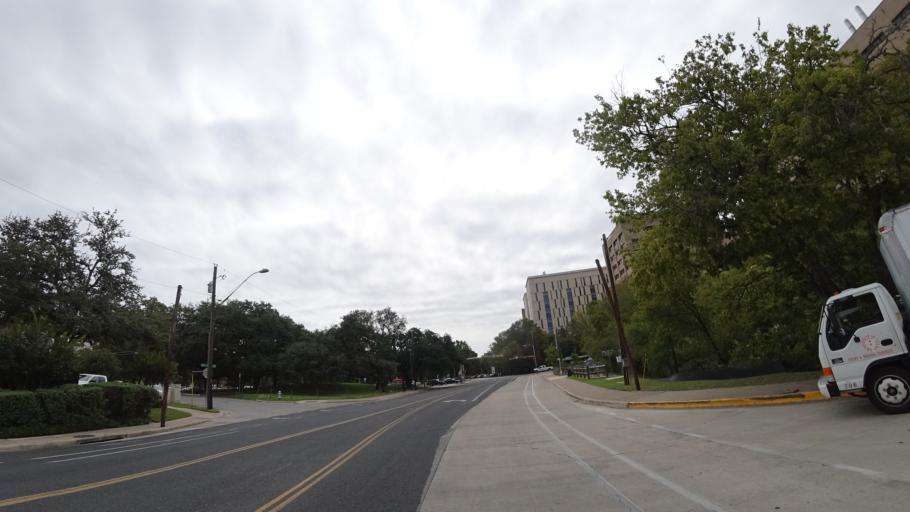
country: US
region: Texas
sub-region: Travis County
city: Austin
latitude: 30.2902
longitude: -97.7345
